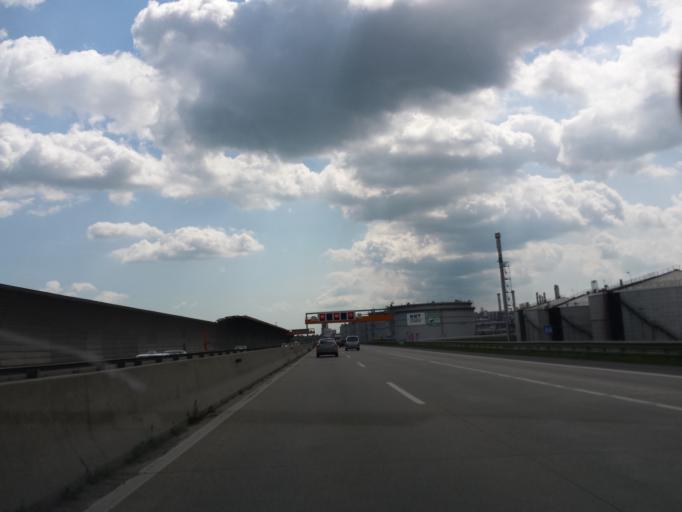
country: AT
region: Lower Austria
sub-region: Politischer Bezirk Wien-Umgebung
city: Schwechat
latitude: 48.1482
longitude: 16.4976
